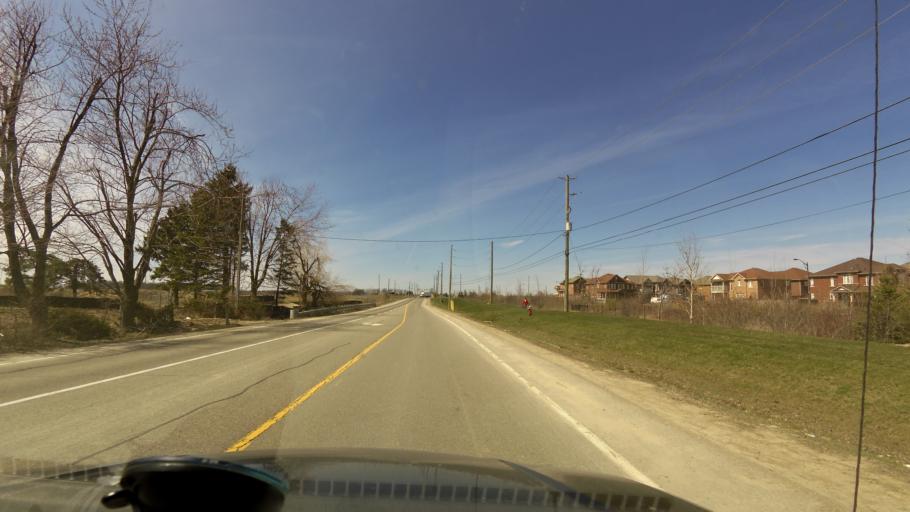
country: CA
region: Ontario
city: Brampton
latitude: 43.7217
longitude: -79.8323
